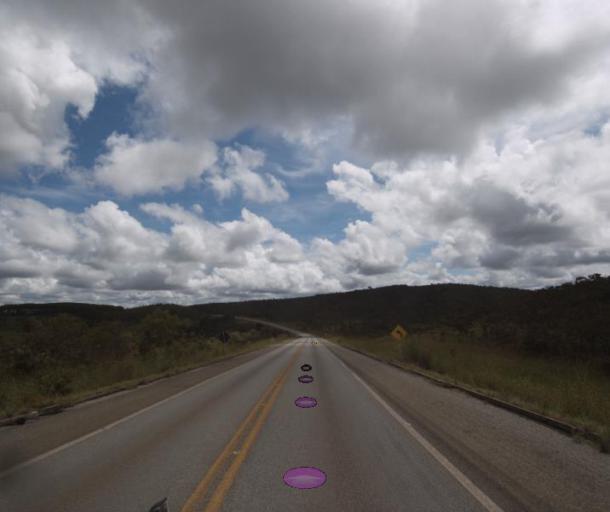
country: BR
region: Goias
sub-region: Pirenopolis
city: Pirenopolis
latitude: -15.7509
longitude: -48.5962
